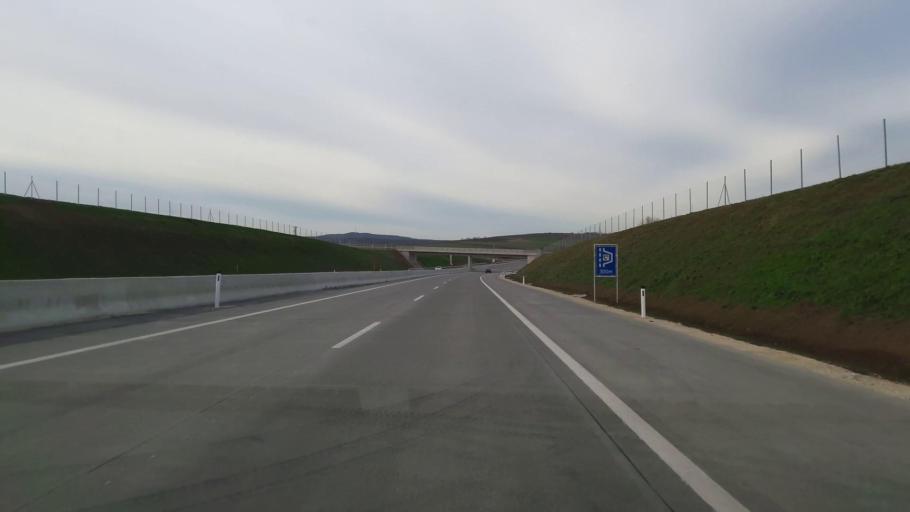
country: AT
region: Lower Austria
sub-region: Politischer Bezirk Mistelbach
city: Herrnbaumgarten
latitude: 48.6790
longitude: 16.6636
